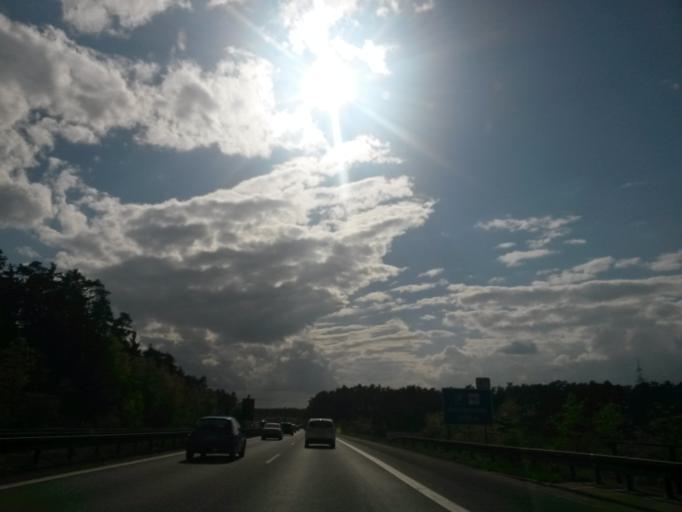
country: DE
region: Bavaria
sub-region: Regierungsbezirk Mittelfranken
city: Rohr
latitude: 49.3146
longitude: 10.8443
